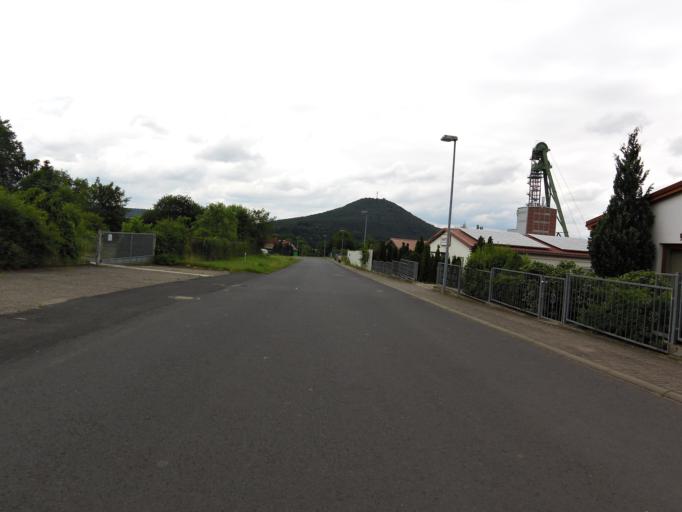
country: DE
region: Thuringia
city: Dorndorf
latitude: 50.8193
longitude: 10.1205
